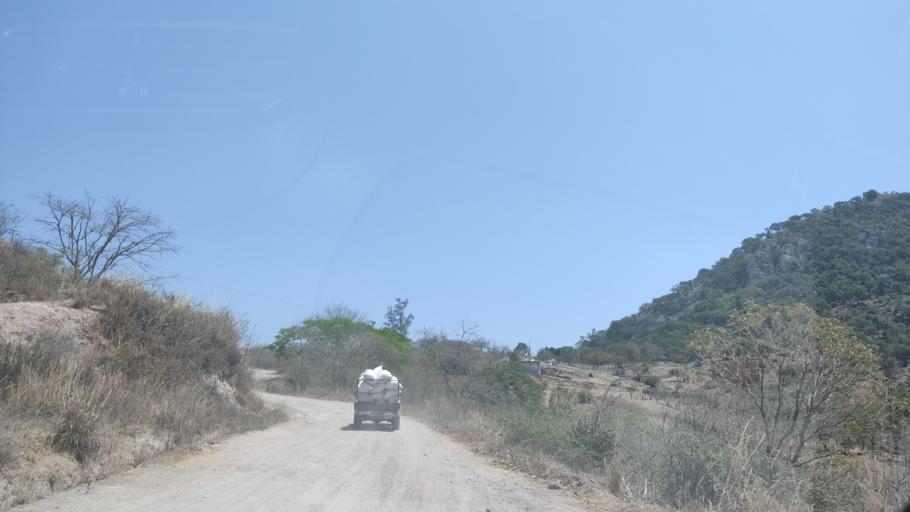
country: MX
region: Nayarit
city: Puga
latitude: 21.6204
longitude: -104.7169
